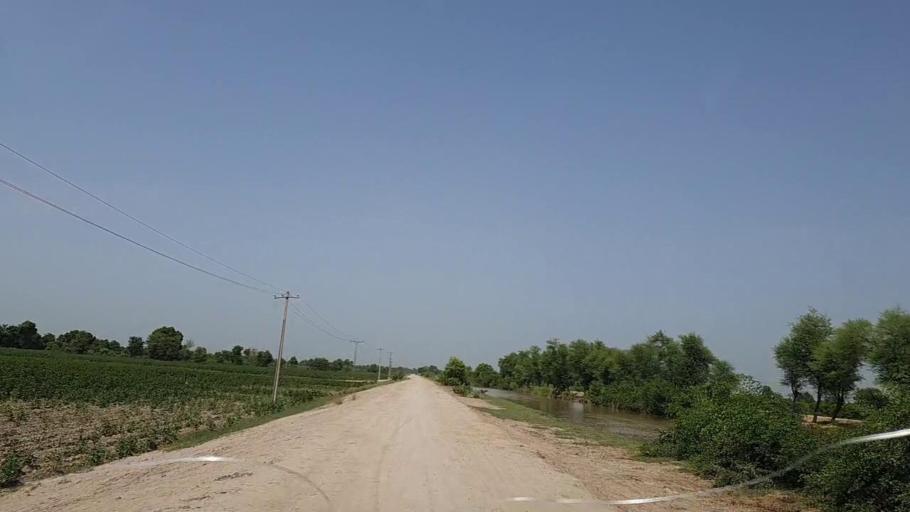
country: PK
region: Sindh
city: Kandiaro
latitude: 27.0433
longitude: 68.1569
